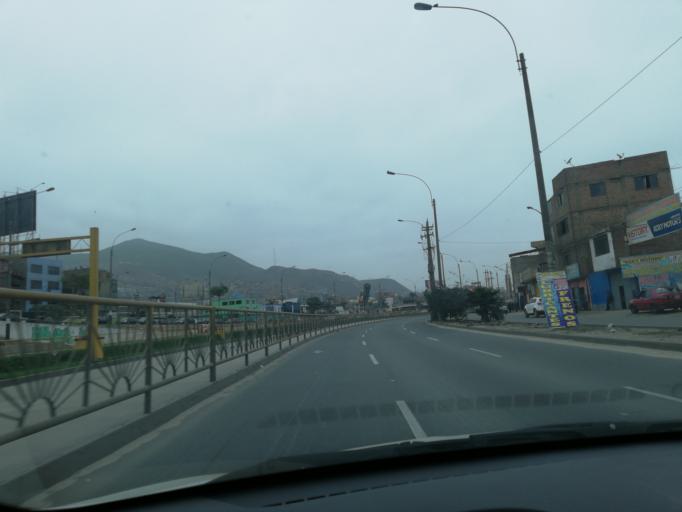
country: PE
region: Lima
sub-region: Lima
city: Independencia
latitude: -11.9953
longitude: -77.0559
